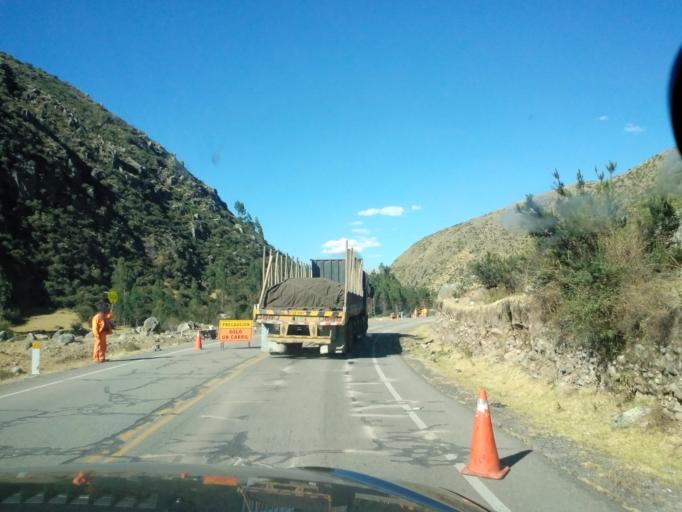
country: PE
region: Ayacucho
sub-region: Provincia de Huamanga
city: Vinchos
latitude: -13.3393
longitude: -74.3857
